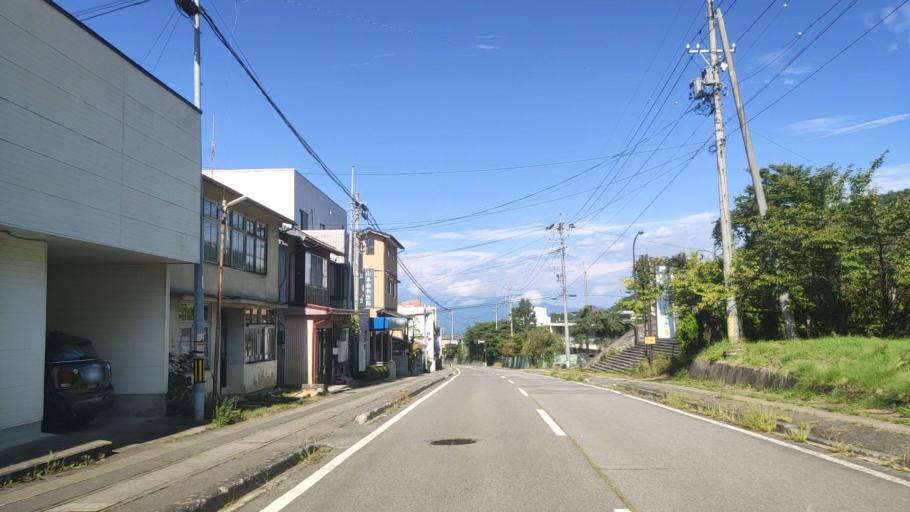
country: JP
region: Nagano
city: Nakano
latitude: 36.7372
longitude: 138.4233
